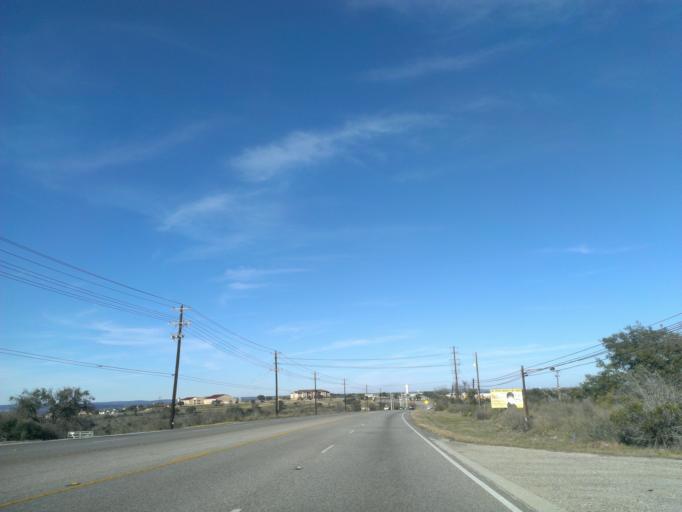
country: US
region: Texas
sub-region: Burnet County
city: Meadowlakes
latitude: 30.5482
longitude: -98.2763
